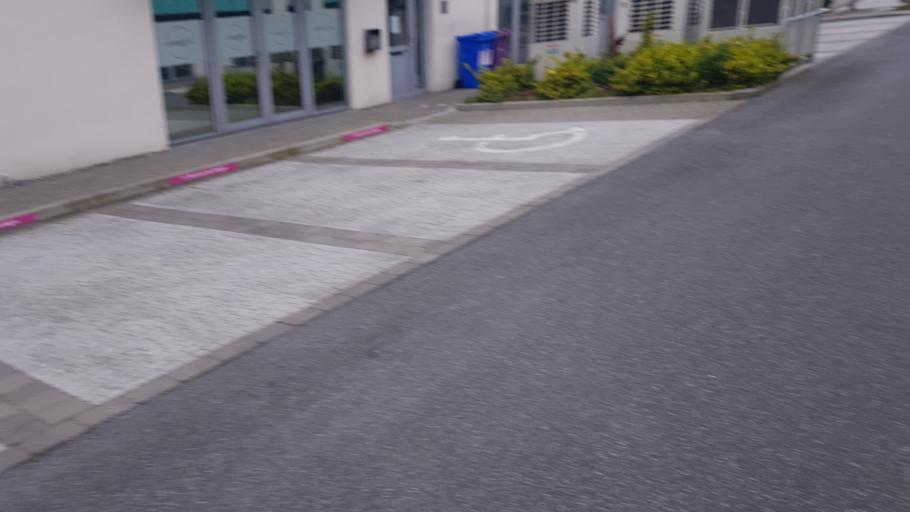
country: IE
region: Leinster
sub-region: Kilkenny
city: Kilkenny
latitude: 52.6358
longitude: -7.2340
